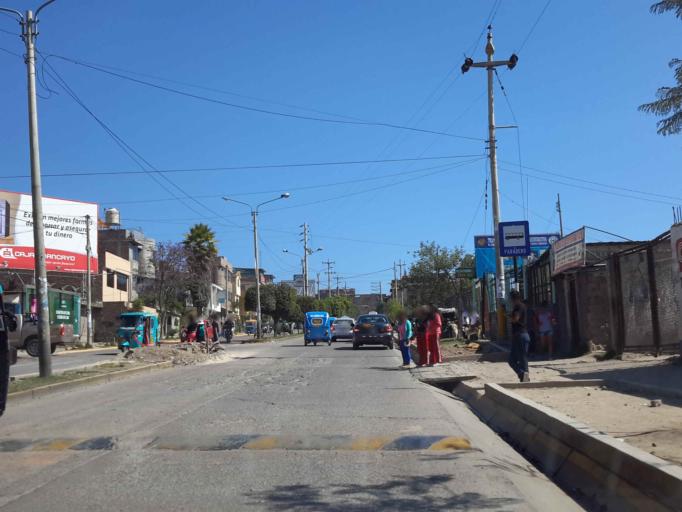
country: PE
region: Ayacucho
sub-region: Provincia de Huamanga
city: Ayacucho
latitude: -13.1467
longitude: -74.2243
